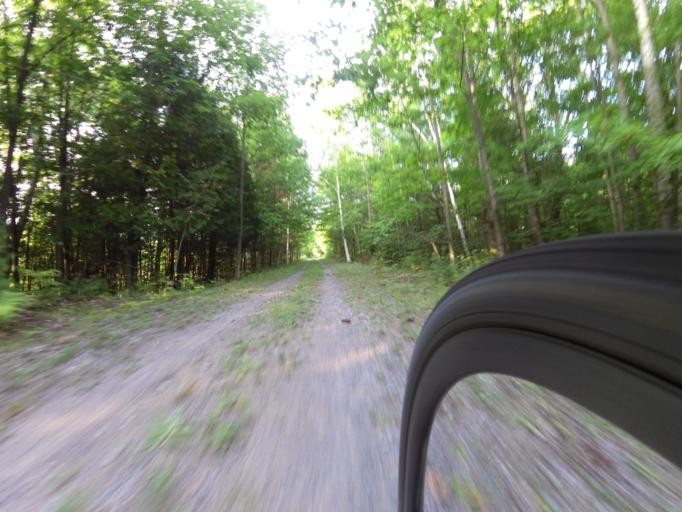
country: CA
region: Ontario
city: Gananoque
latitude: 44.5718
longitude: -76.3455
